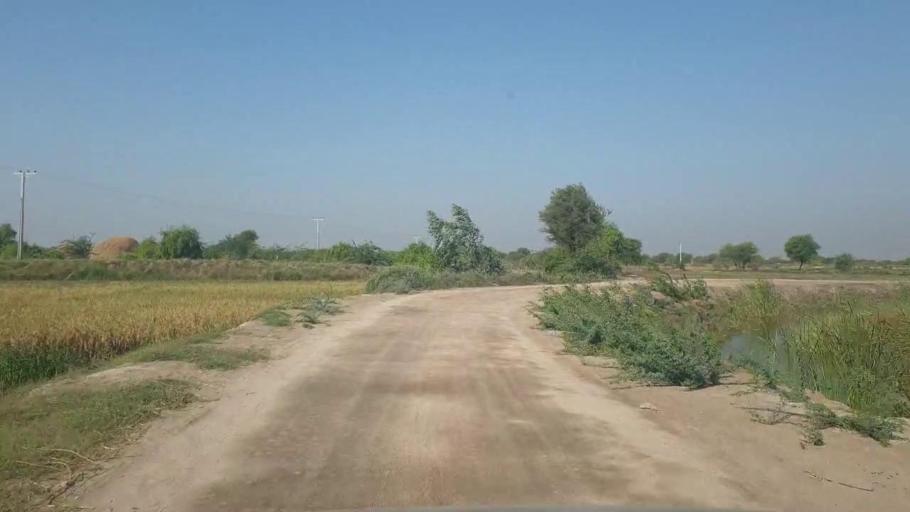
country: PK
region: Sindh
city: Tando Bago
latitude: 24.7360
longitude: 68.8892
